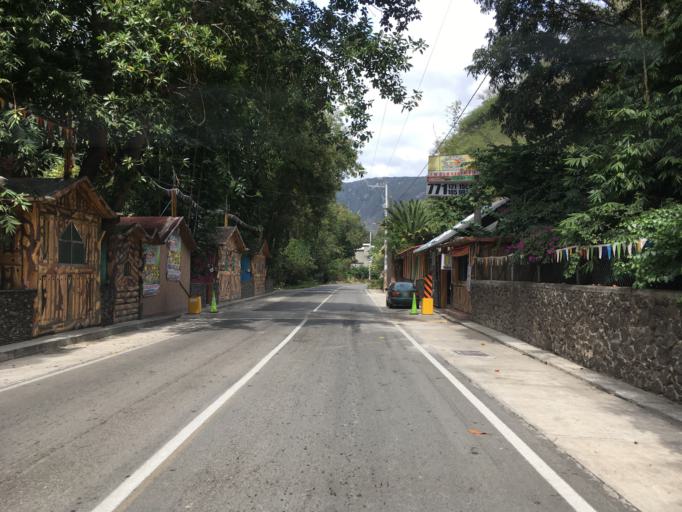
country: MX
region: Hidalgo
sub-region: San Agustin Metzquititlan
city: Mezquititlan
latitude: 20.5264
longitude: -98.7240
